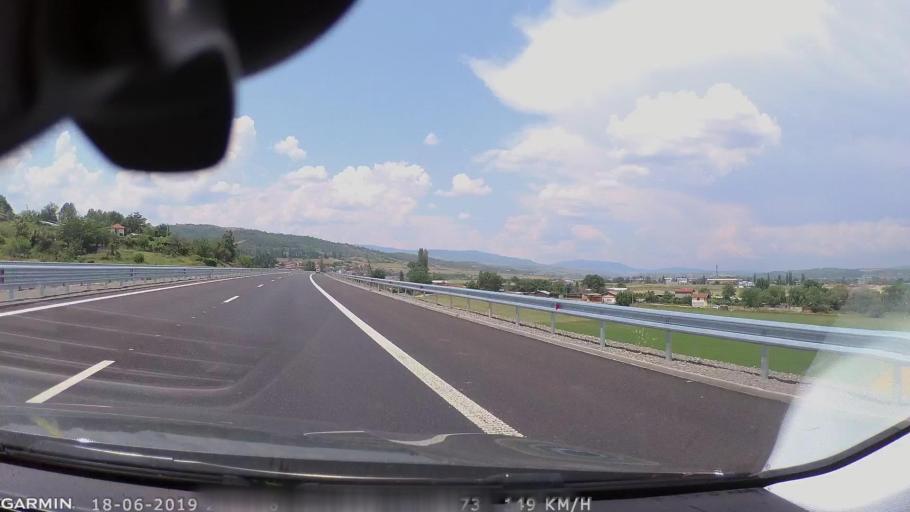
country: BG
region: Blagoevgrad
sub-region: Obshtina Blagoevgrad
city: Blagoevgrad
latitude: 41.9745
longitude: 23.0758
